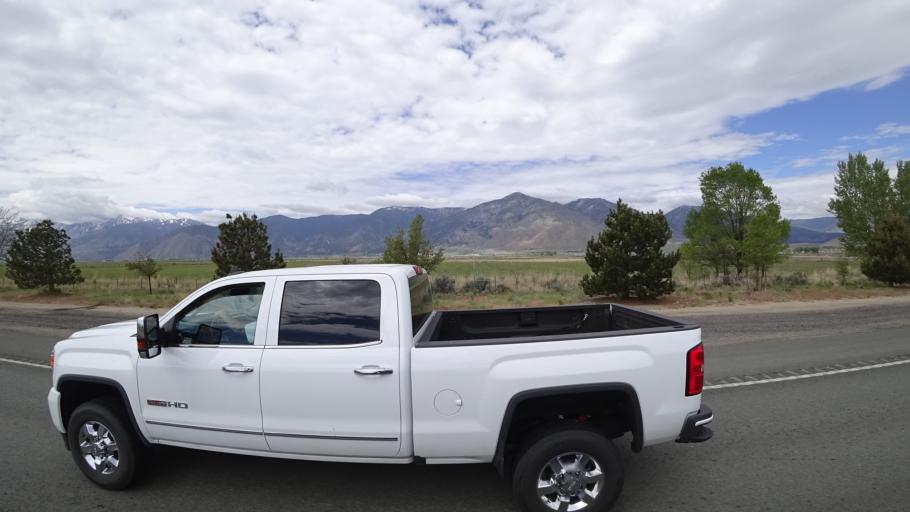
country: US
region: Nevada
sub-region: Douglas County
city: Indian Hills
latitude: 39.0321
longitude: -119.7801
